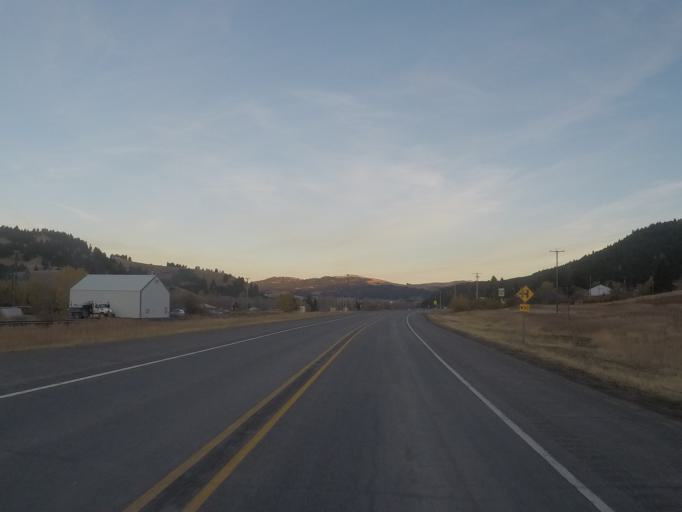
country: US
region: Montana
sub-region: Lewis and Clark County
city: Helena West Side
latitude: 46.5627
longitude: -112.4358
